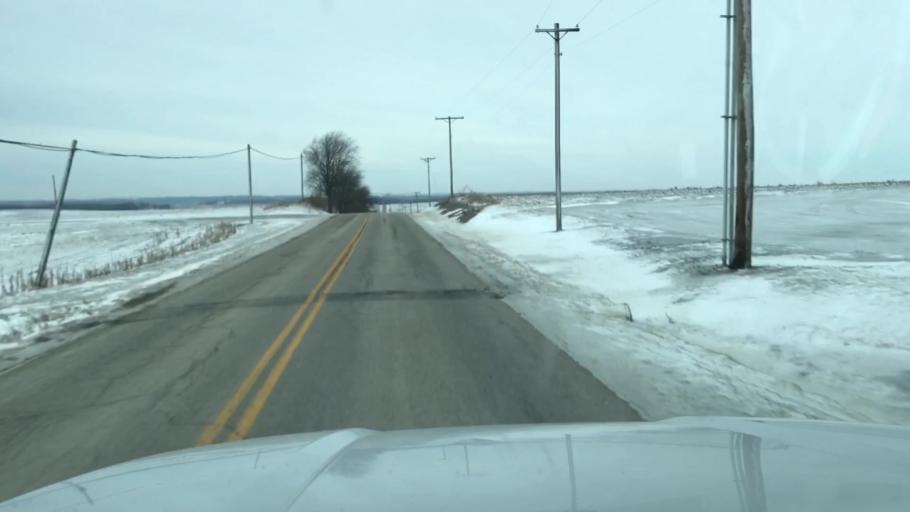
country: US
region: Missouri
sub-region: Andrew County
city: Savannah
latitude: 40.0248
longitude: -94.9398
